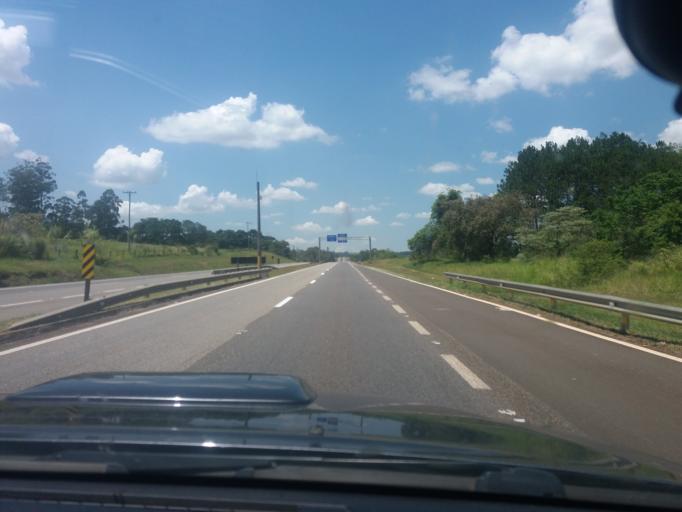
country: BR
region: Sao Paulo
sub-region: Tatui
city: Tatui
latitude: -23.4622
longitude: -47.9618
